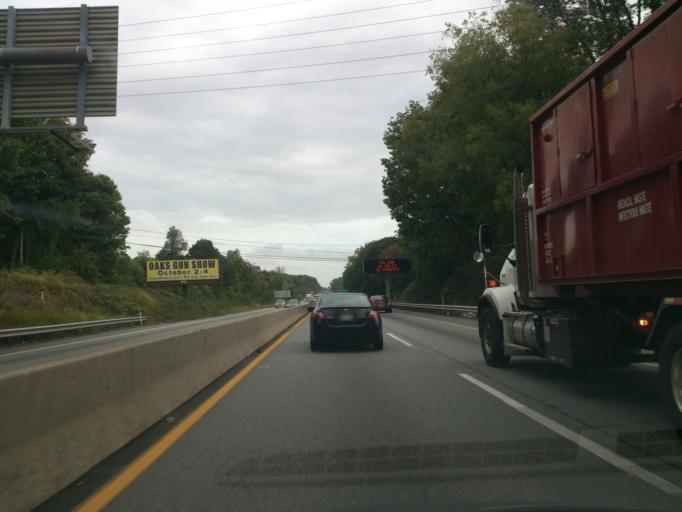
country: US
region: Pennsylvania
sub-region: Berks County
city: Kenhorst
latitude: 40.3114
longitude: -75.9157
